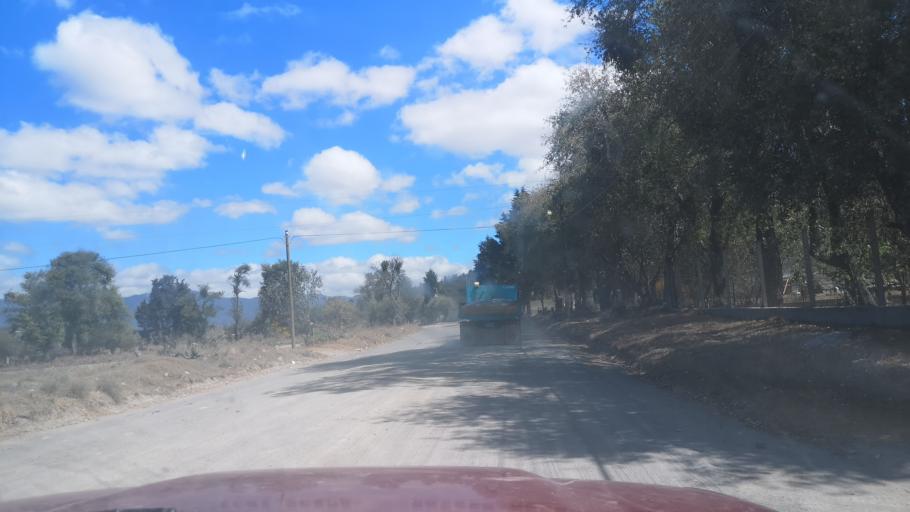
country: GT
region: Quetzaltenango
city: Quetzaltenango
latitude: 14.8062
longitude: -91.5356
